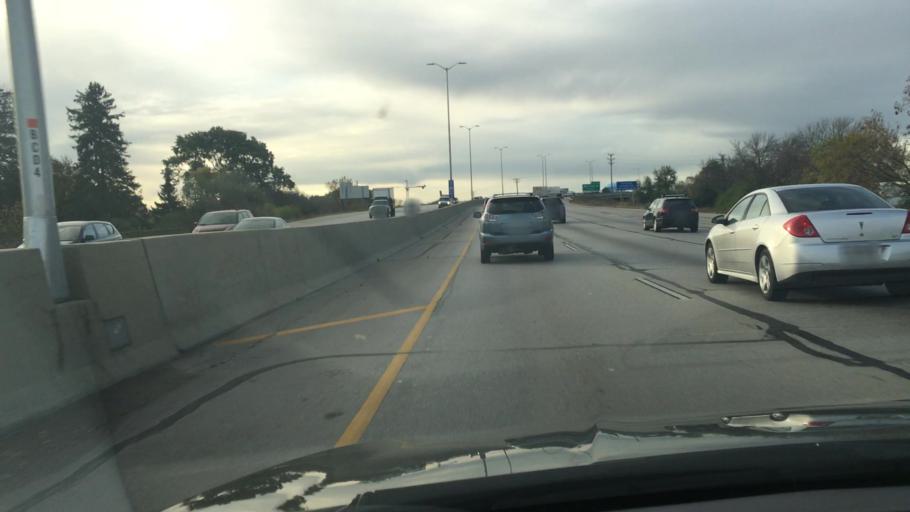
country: US
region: Wisconsin
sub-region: Waukesha County
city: Butler
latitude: 43.0863
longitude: -88.0575
